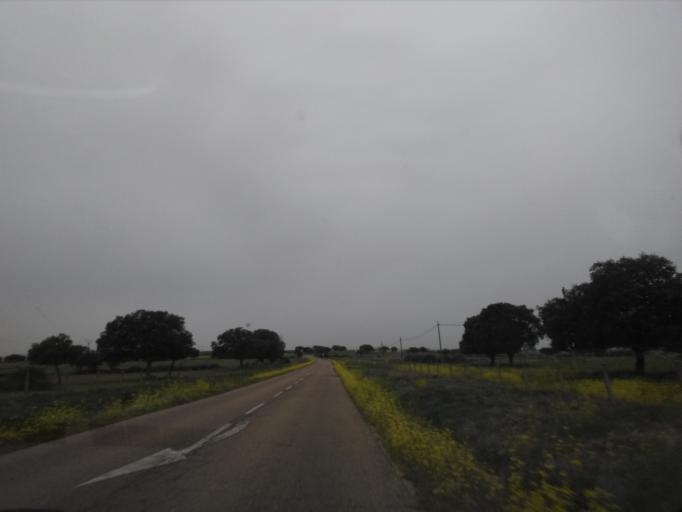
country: ES
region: Castille and Leon
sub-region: Provincia de Salamanca
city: Yecla de Yeltes
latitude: 40.9799
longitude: -6.4680
